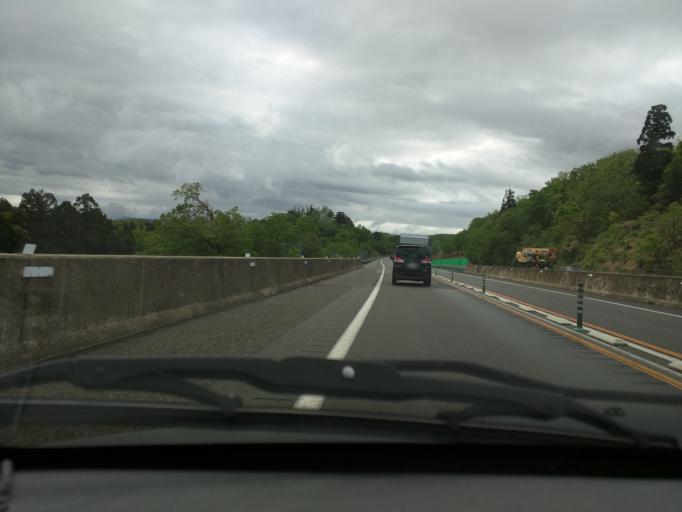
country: JP
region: Niigata
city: Joetsu
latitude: 37.1193
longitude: 138.2149
